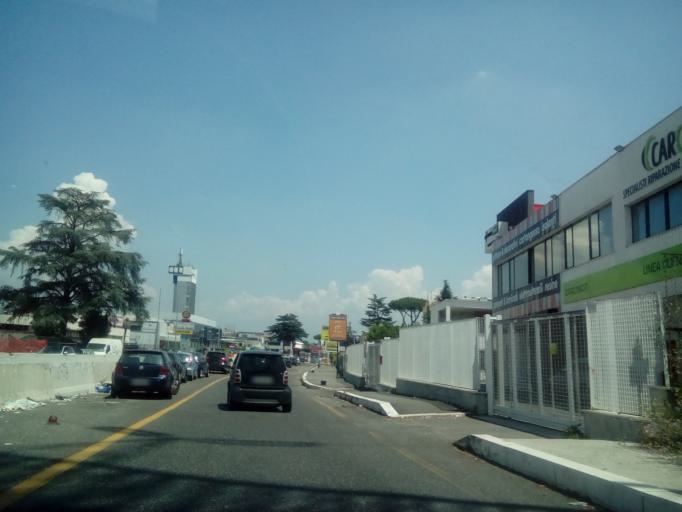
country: IT
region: Latium
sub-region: Citta metropolitana di Roma Capitale
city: Colle Verde
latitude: 41.9328
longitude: 12.5878
